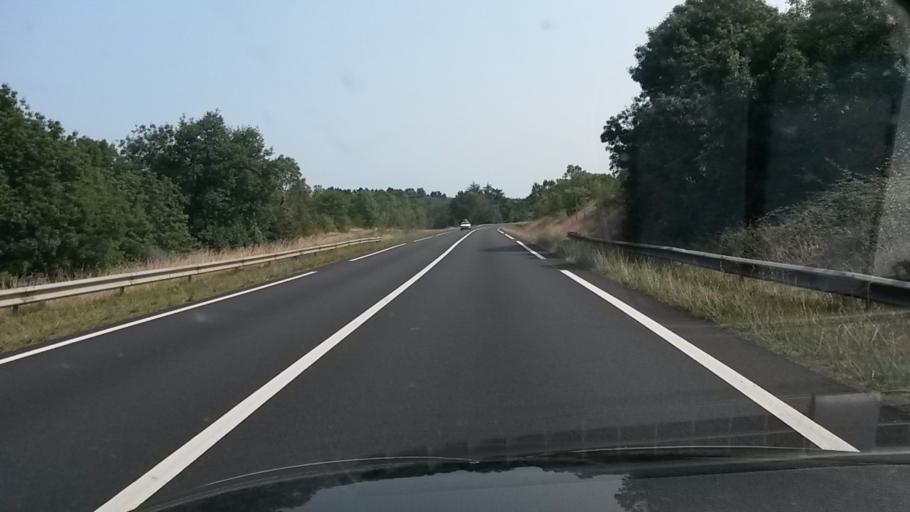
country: FR
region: Pays de la Loire
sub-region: Departement de la Loire-Atlantique
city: Ancenis
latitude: 47.3761
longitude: -1.1694
